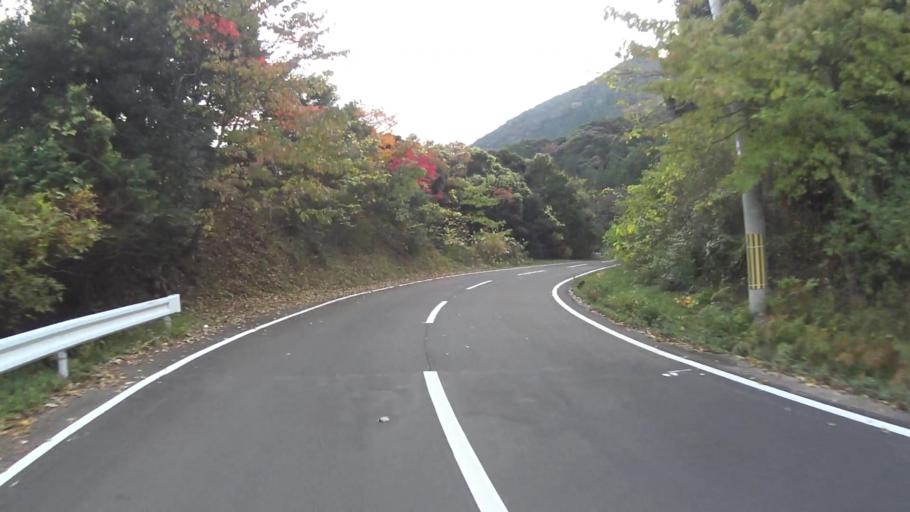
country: JP
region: Kyoto
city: Maizuru
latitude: 35.5696
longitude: 135.4505
